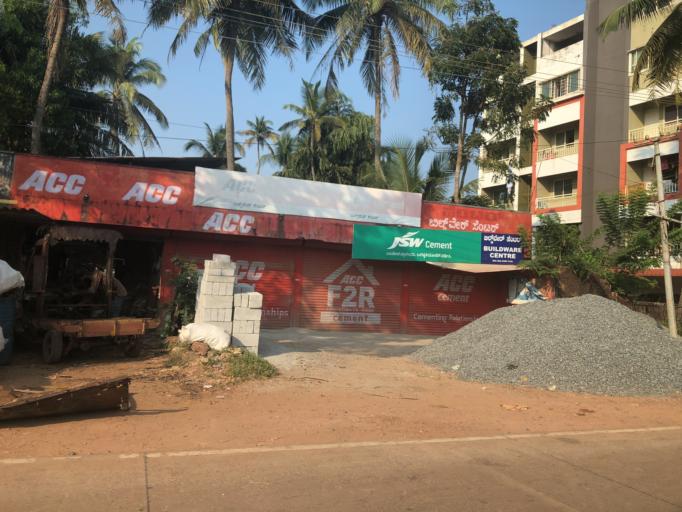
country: IN
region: Karnataka
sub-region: Dakshina Kannada
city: Ullal
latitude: 12.8166
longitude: 74.8477
